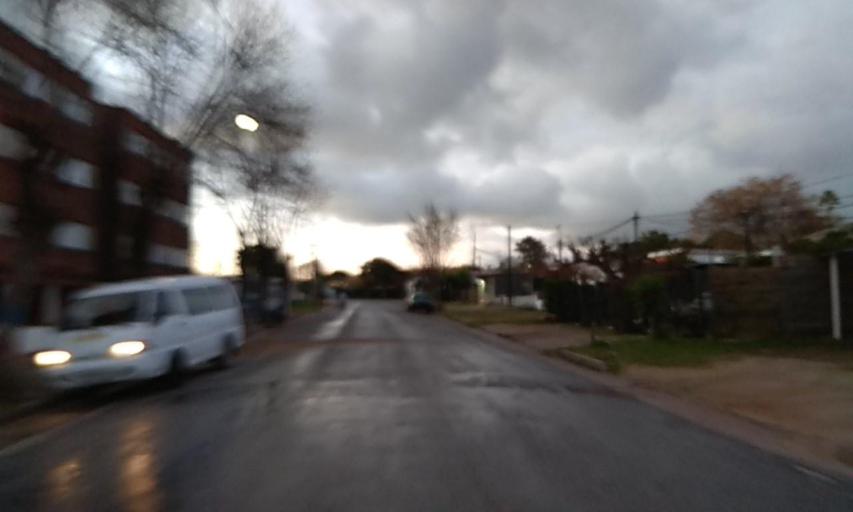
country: UY
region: Florida
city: Florida
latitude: -34.1085
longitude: -56.2131
